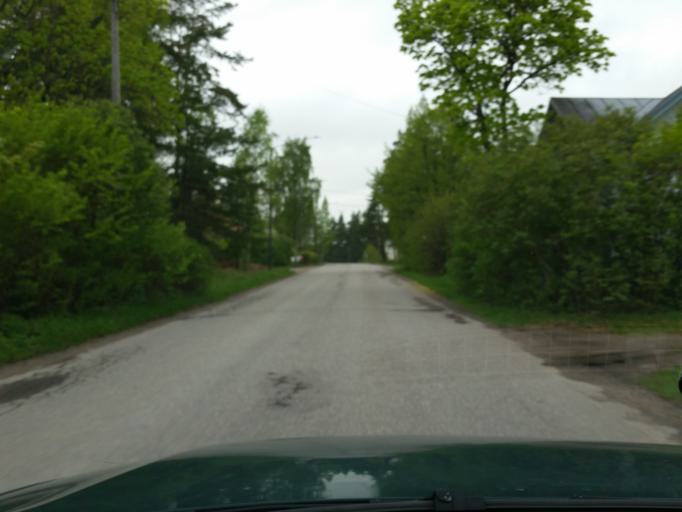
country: FI
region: Uusimaa
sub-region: Raaseporin
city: Inga
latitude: 60.1365
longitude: 23.8662
